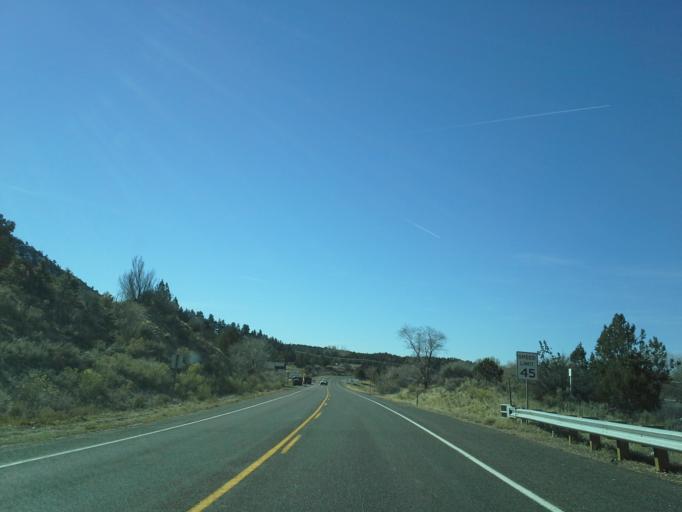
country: US
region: Utah
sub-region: Kane County
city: Kanab
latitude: 37.2803
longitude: -112.6281
